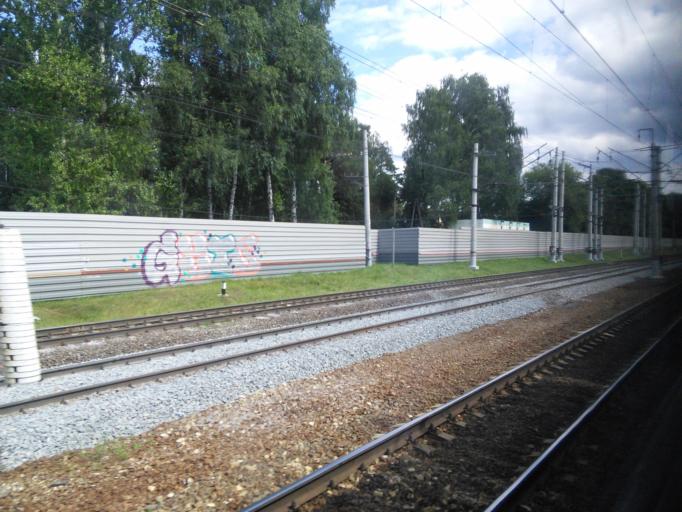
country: RU
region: Moskovskaya
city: Malakhovka
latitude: 55.6375
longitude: 38.0356
